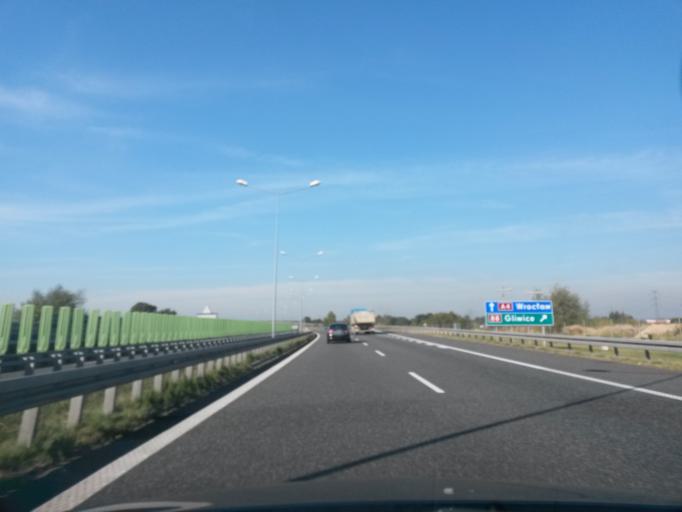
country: PL
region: Silesian Voivodeship
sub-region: Powiat gliwicki
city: Sosnicowice
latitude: 50.3413
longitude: 18.5435
